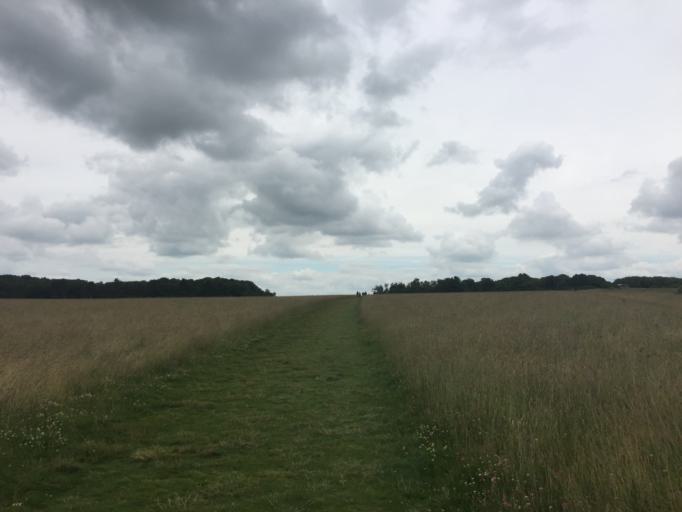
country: GB
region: England
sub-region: Wiltshire
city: Winterbourne Stoke
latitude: 51.1844
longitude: -1.8502
